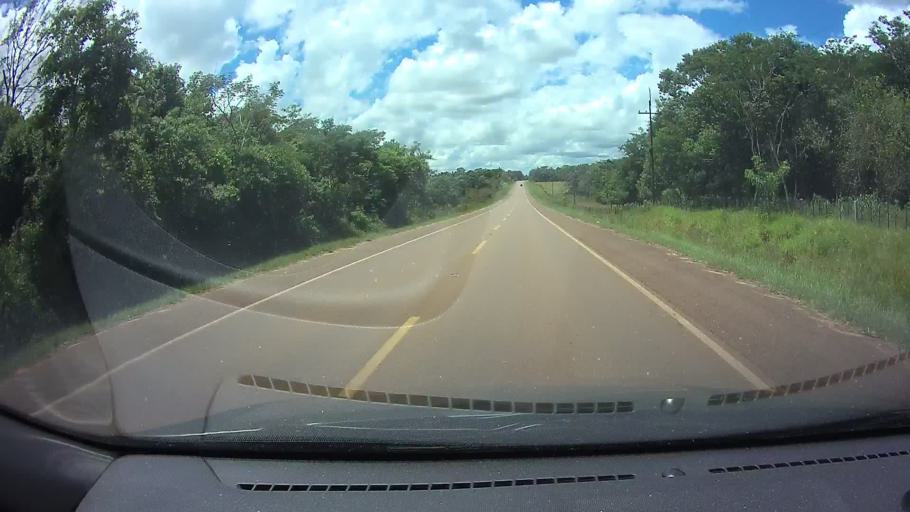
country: PY
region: Paraguari
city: La Colmena
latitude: -25.8910
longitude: -56.8107
